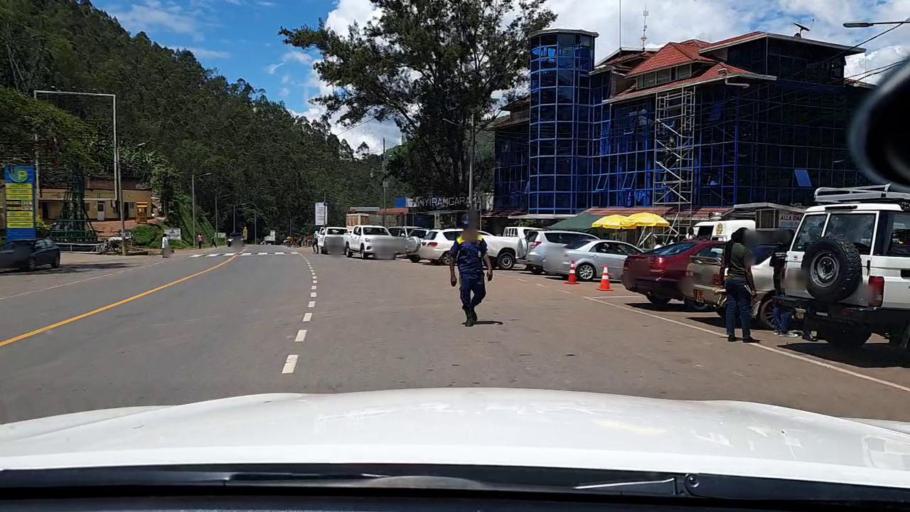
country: RW
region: Northern Province
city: Byumba
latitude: -1.6632
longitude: 29.8875
